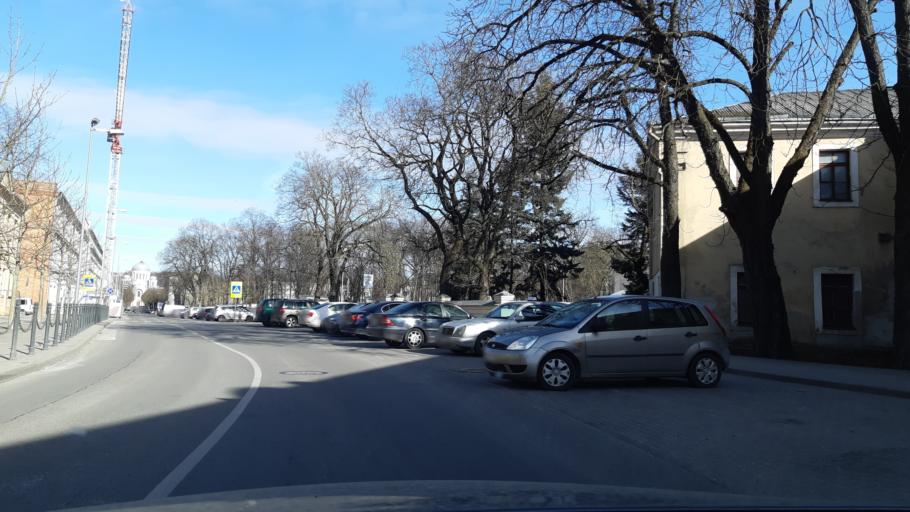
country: LT
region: Kauno apskritis
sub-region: Kaunas
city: Aleksotas
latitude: 54.8898
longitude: 23.9206
